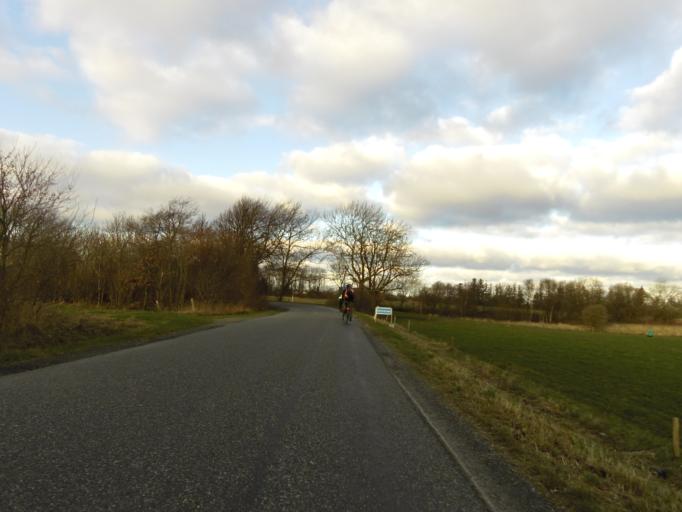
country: DK
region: South Denmark
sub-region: Esbjerg Kommune
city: Ribe
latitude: 55.3047
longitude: 8.8485
